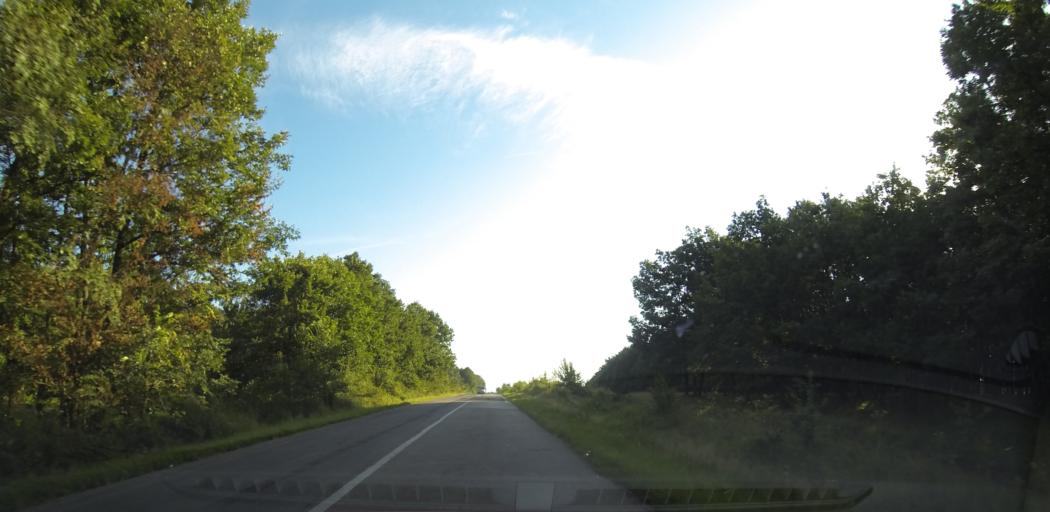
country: RO
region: Valcea
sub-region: Comuna Balcesti
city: Balcesti
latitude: 44.5958
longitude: 23.9259
